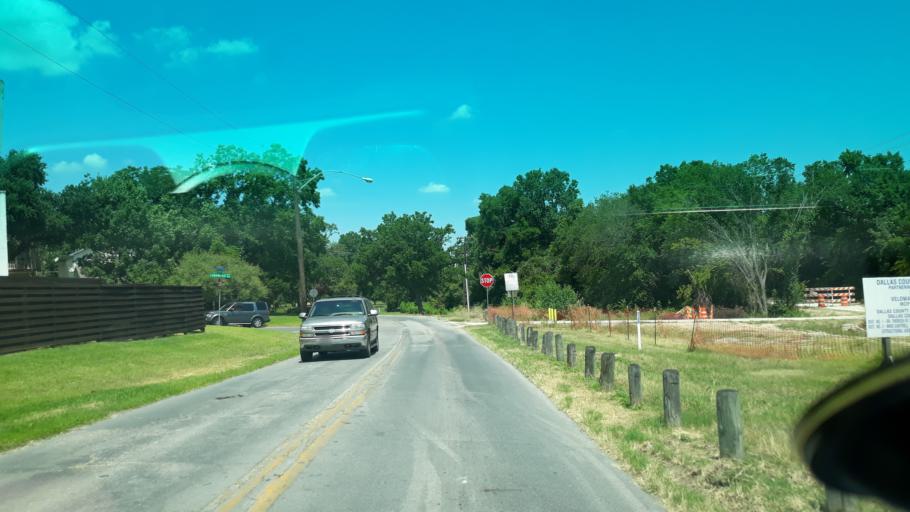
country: US
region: Texas
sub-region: Dallas County
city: Highland Park
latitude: 32.8242
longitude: -96.7319
